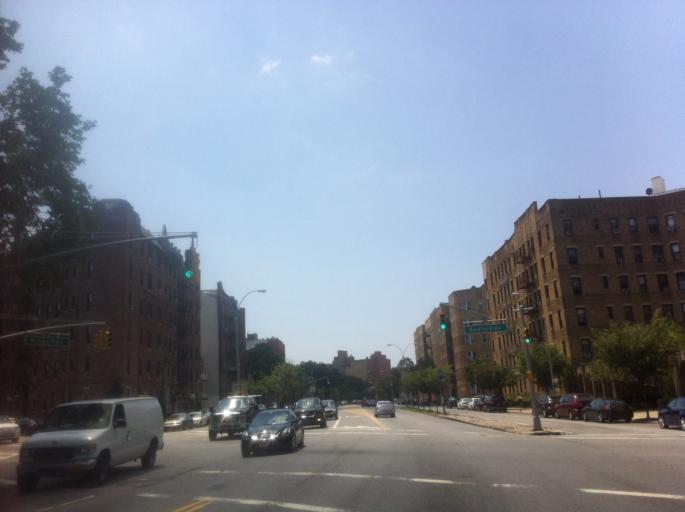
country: US
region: New York
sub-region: Kings County
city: Brooklyn
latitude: 40.6140
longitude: -73.9478
